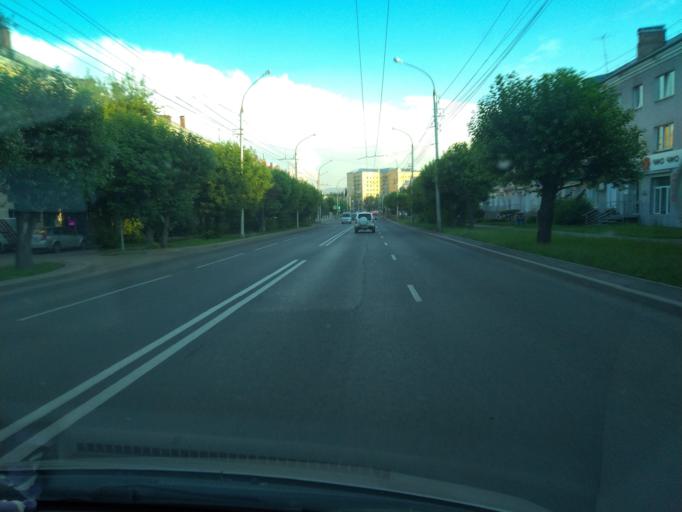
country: RU
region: Krasnoyarskiy
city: Krasnoyarsk
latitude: 56.0291
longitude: 92.9074
